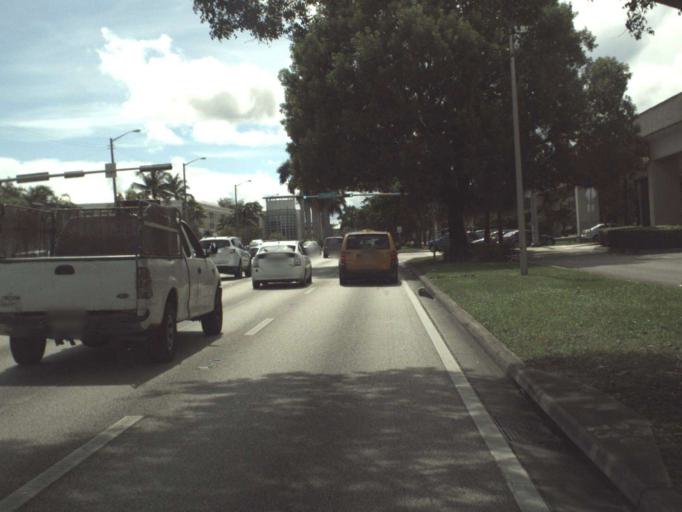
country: US
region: Florida
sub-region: Miami-Dade County
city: Coral Gables
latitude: 25.7126
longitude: -80.2795
